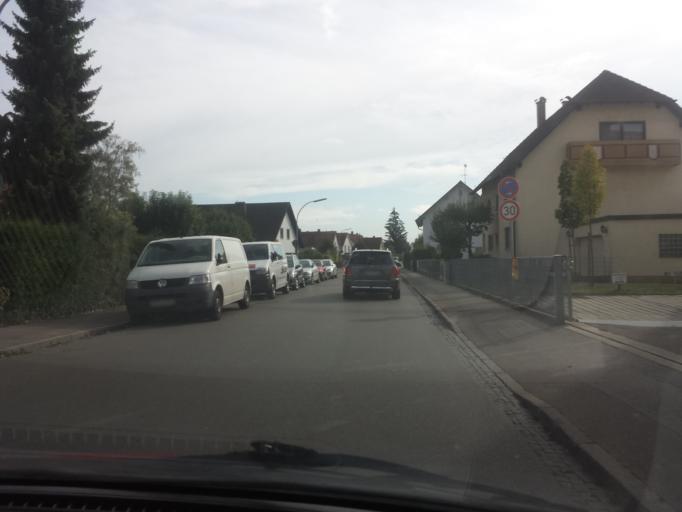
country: DE
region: Bavaria
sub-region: Upper Bavaria
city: Neuburg an der Donau
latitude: 48.7306
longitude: 11.2006
